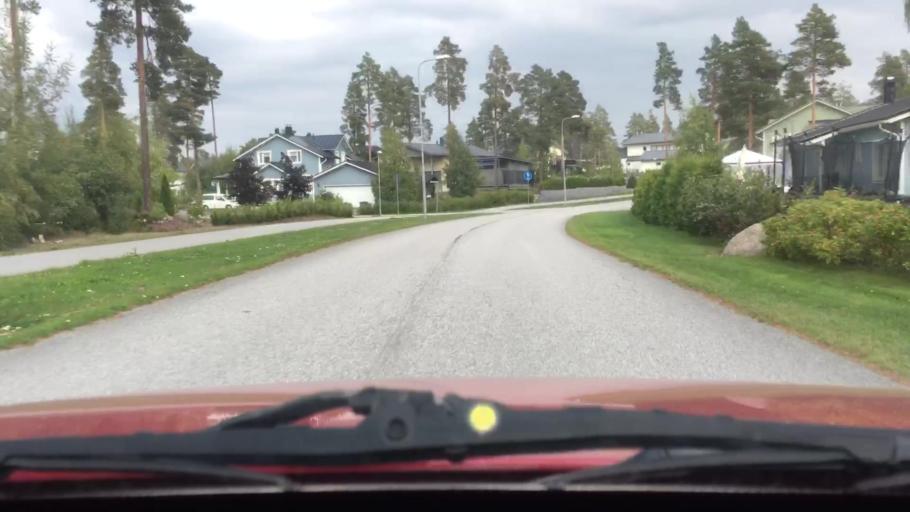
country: FI
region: Varsinais-Suomi
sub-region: Turku
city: Masku
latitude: 60.5594
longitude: 22.1369
